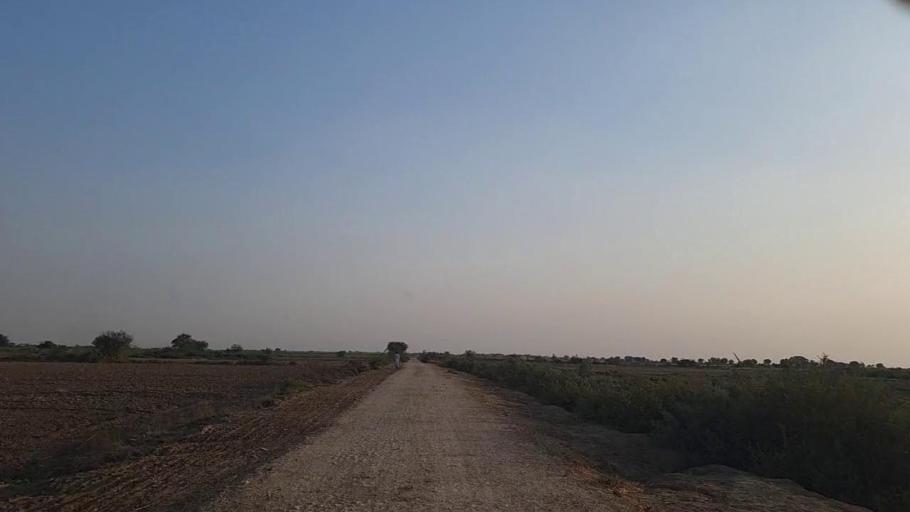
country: PK
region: Sindh
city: Jati
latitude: 24.4827
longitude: 68.4132
